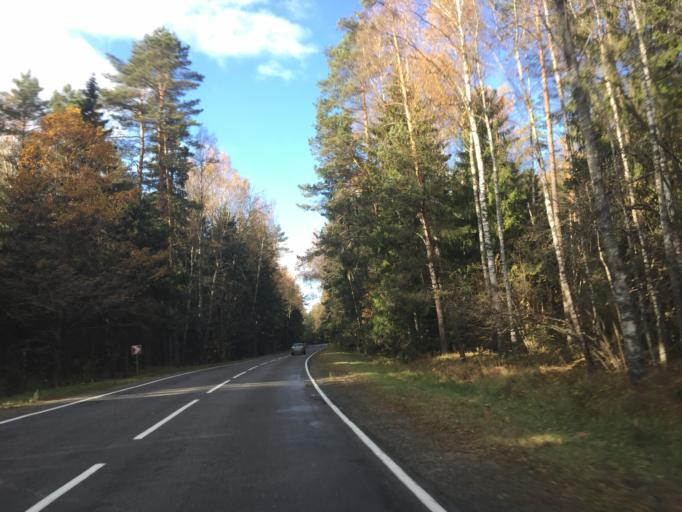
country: BY
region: Minsk
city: Svir
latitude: 54.9225
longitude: 26.5104
